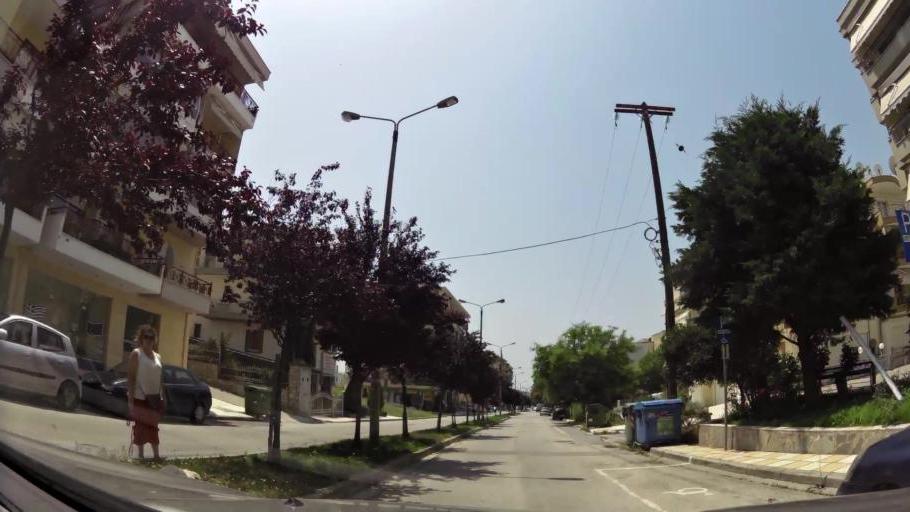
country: GR
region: Central Macedonia
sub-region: Nomos Thessalonikis
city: Evosmos
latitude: 40.6759
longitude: 22.8998
